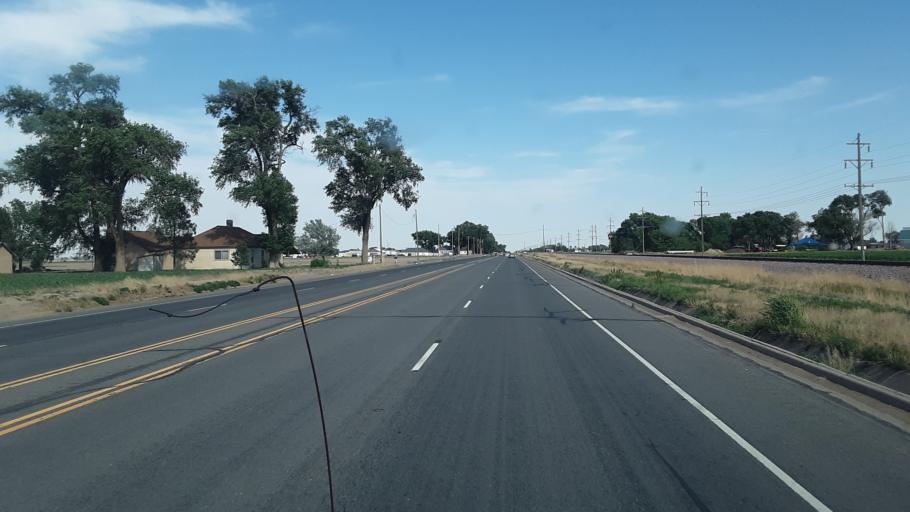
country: US
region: Colorado
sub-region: Otero County
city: Rocky Ford
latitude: 38.0749
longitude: -103.7744
